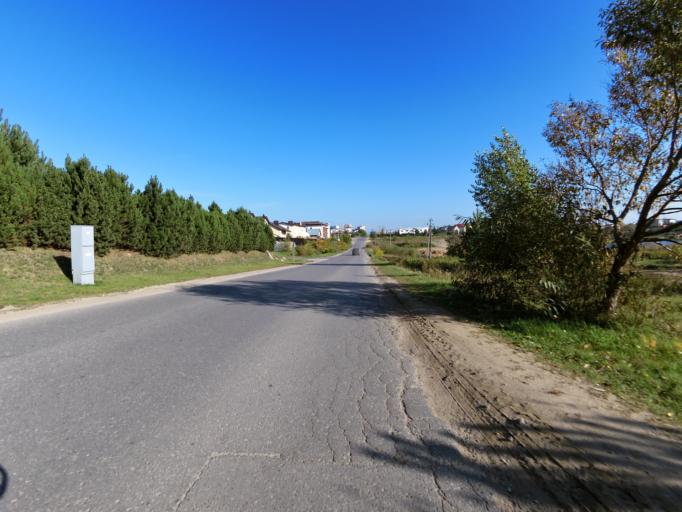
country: LT
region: Vilnius County
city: Pasilaiciai
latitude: 54.7359
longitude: 25.1971
